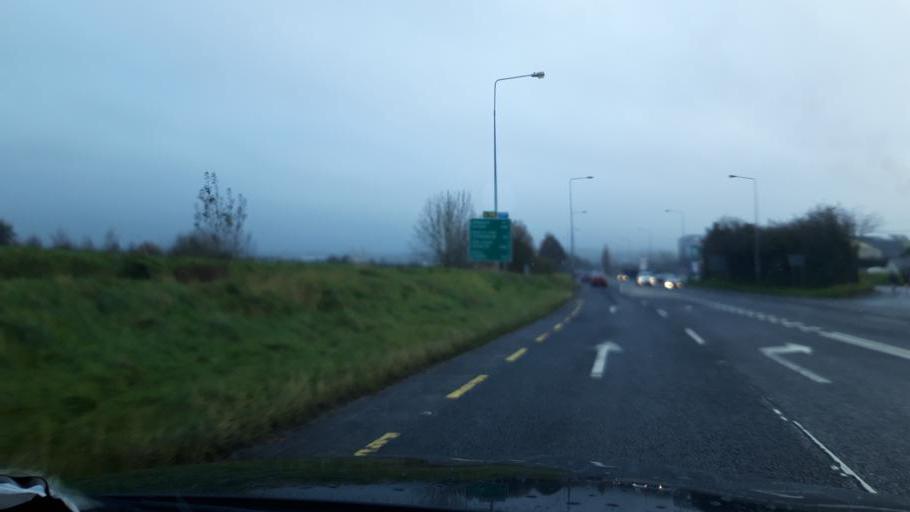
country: IE
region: Ulster
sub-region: County Donegal
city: Letterkenny
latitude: 54.9476
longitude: -7.7122
